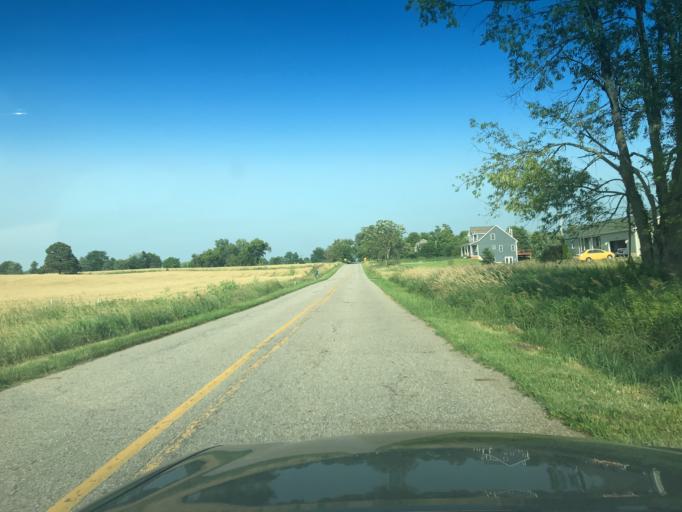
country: US
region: Michigan
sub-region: Ingham County
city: Mason
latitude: 42.5531
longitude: -84.4684
